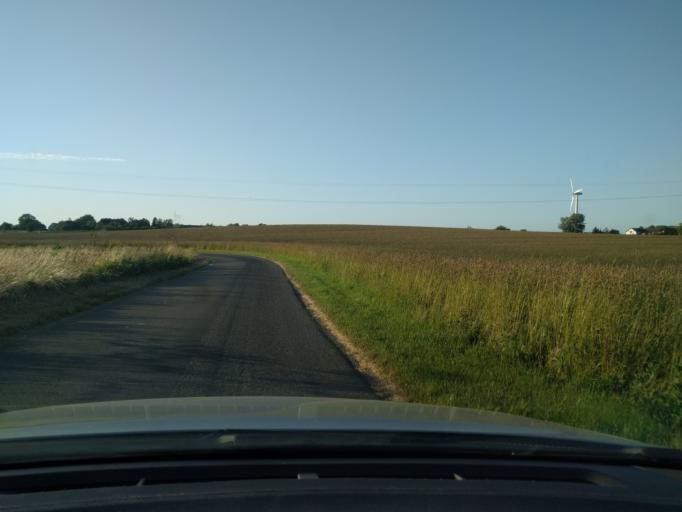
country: DK
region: Zealand
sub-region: Vordingborg Kommune
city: Stege
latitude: 54.9627
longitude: 12.2364
